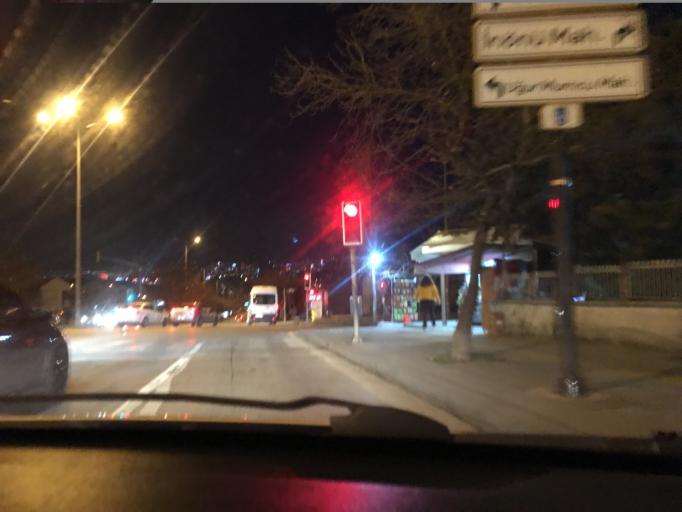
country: TR
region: Ankara
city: Batikent
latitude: 39.9544
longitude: 32.7325
